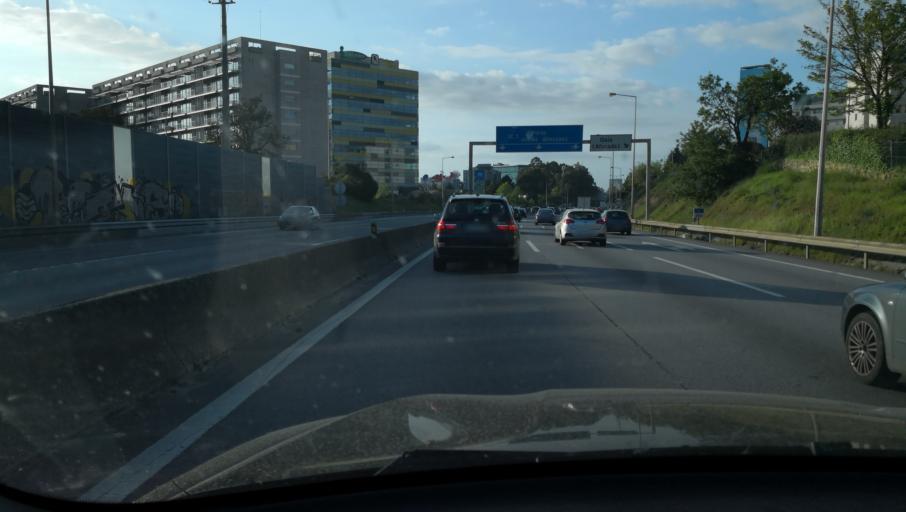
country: PT
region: Porto
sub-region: Vila Nova de Gaia
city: Canidelo
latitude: 41.1407
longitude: -8.6382
